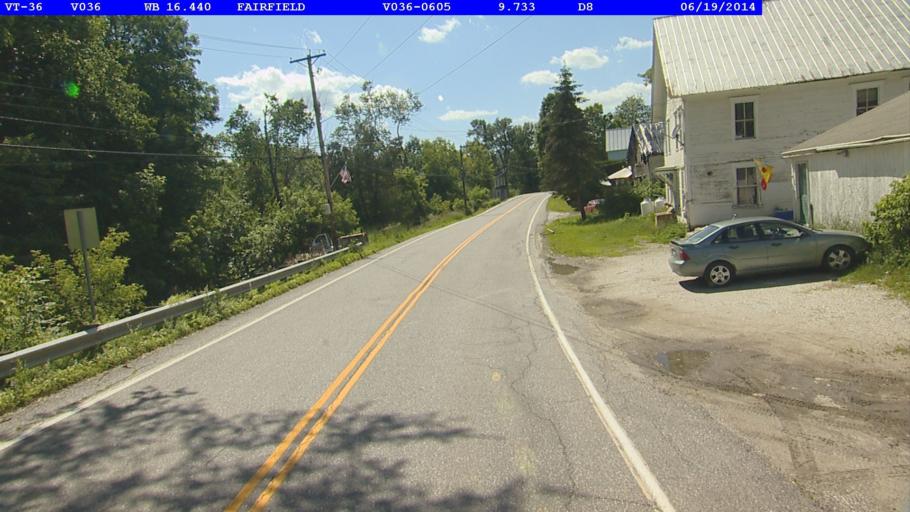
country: US
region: Vermont
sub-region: Franklin County
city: Enosburg Falls
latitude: 44.7830
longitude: -72.8544
